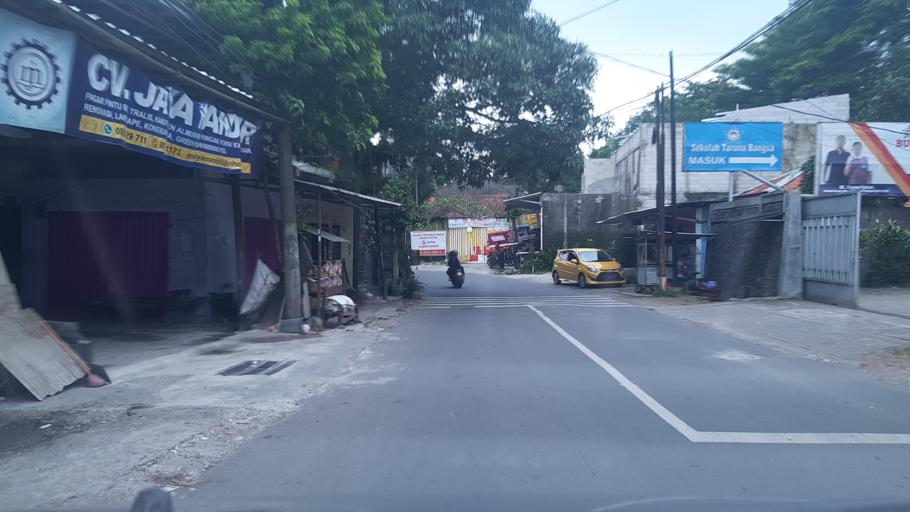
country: ID
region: West Java
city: Bogor
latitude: -6.5700
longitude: 106.8653
